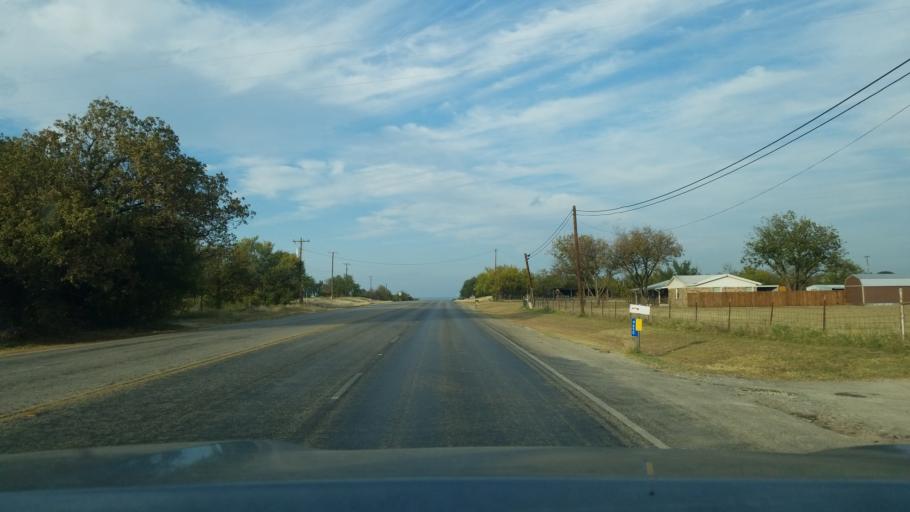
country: US
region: Texas
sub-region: Brown County
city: Early
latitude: 31.7692
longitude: -98.9535
